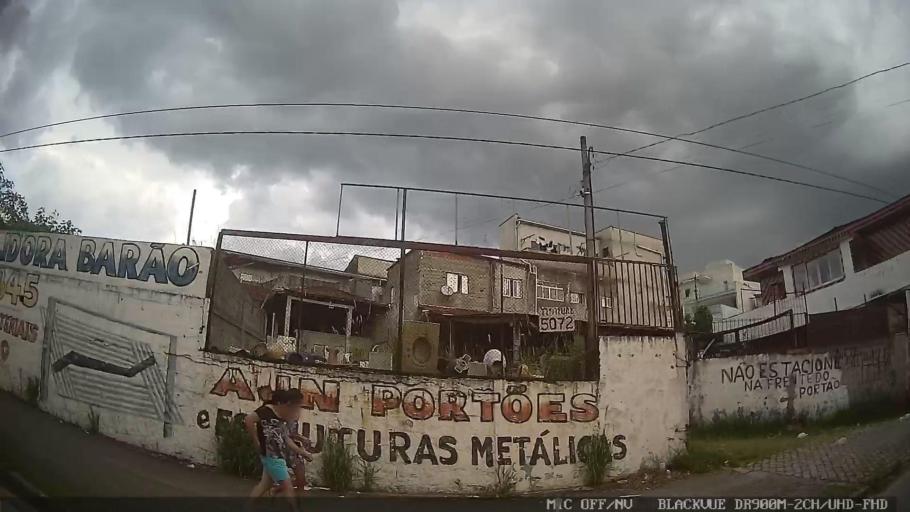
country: BR
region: Sao Paulo
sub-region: Ribeirao Pires
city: Ribeirao Pires
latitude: -23.6755
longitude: -46.4188
